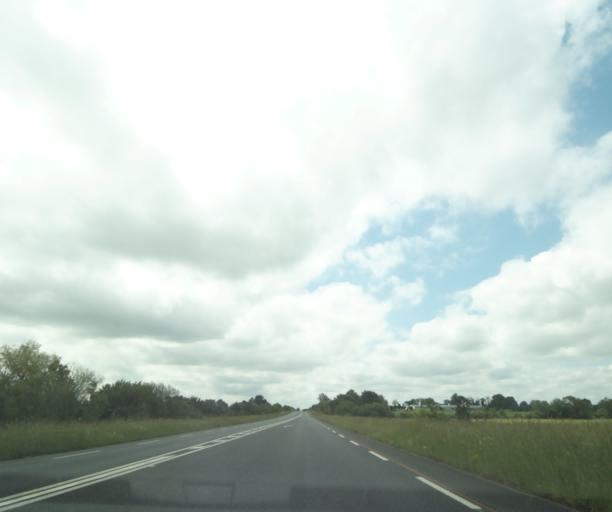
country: FR
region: Poitou-Charentes
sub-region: Departement des Deux-Sevres
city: Airvault
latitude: 46.7872
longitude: -0.2157
